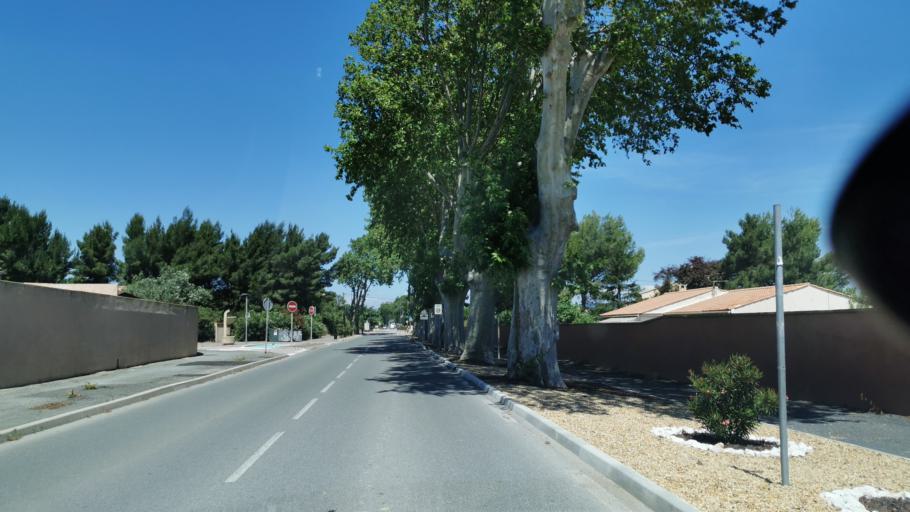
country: FR
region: Languedoc-Roussillon
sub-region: Departement de l'Aude
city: Saint-Marcel-sur-Aude
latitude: 43.2459
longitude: 2.9199
